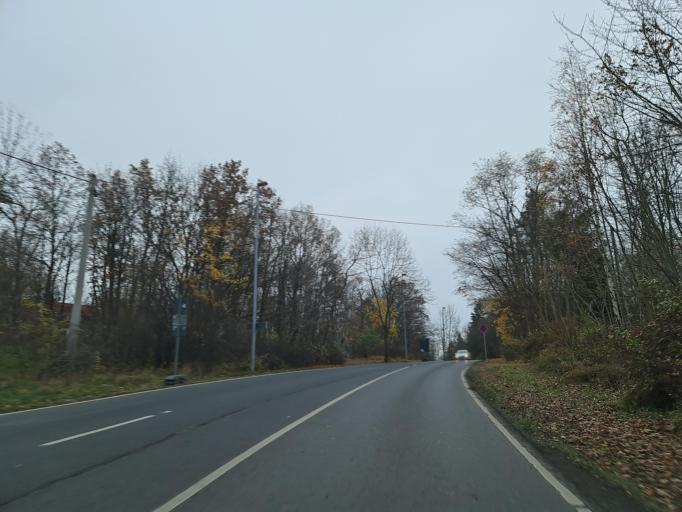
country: DE
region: Saxony
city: Plauen
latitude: 50.5019
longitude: 12.1027
